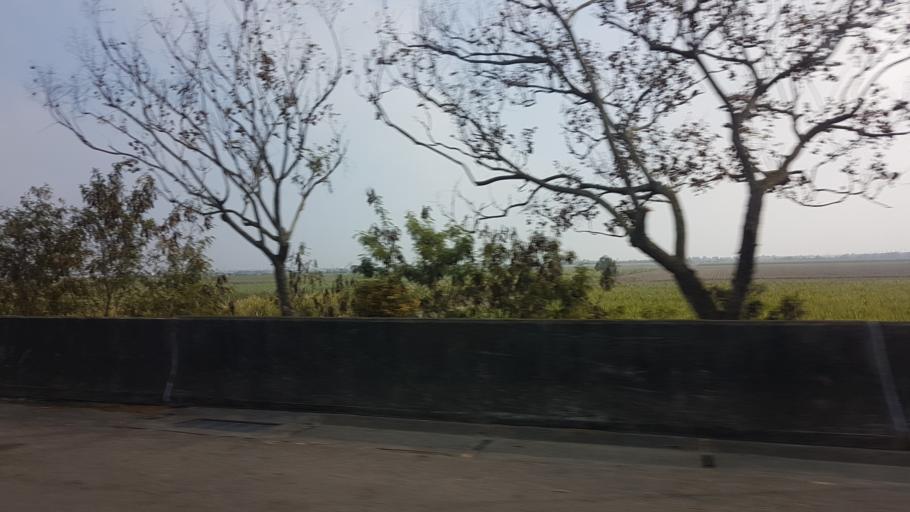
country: TW
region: Taiwan
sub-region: Chiayi
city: Taibao
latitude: 23.4285
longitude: 120.3271
